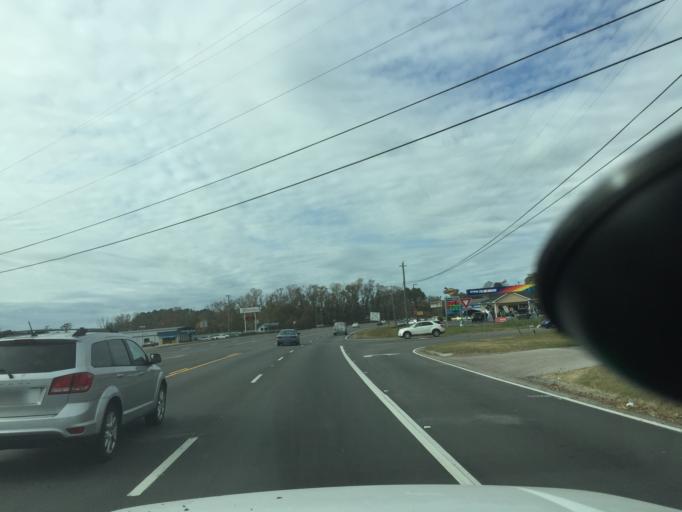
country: US
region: Georgia
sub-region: Chatham County
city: Garden City
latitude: 32.0865
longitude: -81.1604
